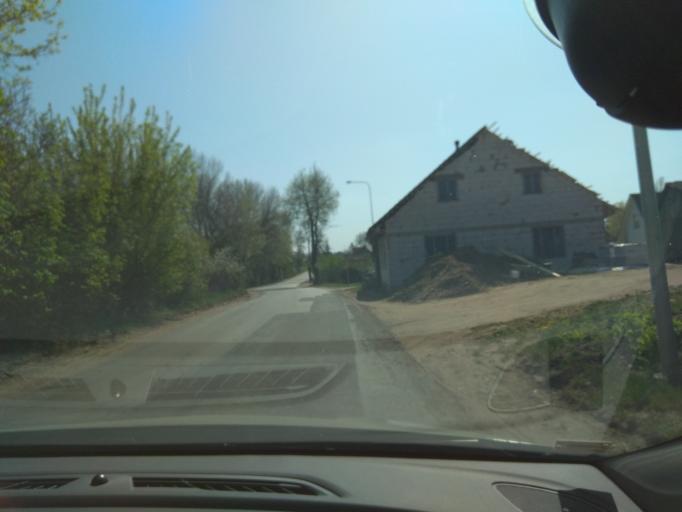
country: LT
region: Panevezys
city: Pasvalys
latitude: 55.9305
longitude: 24.2398
